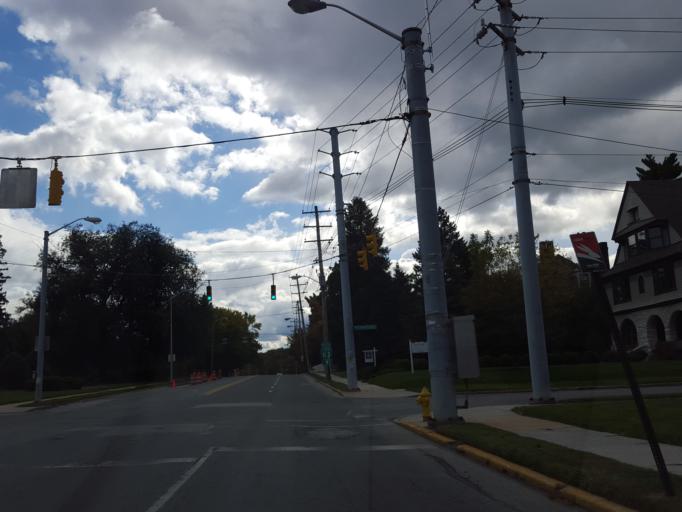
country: US
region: Pennsylvania
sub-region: York County
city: Grantley
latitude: 39.9507
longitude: -76.7224
